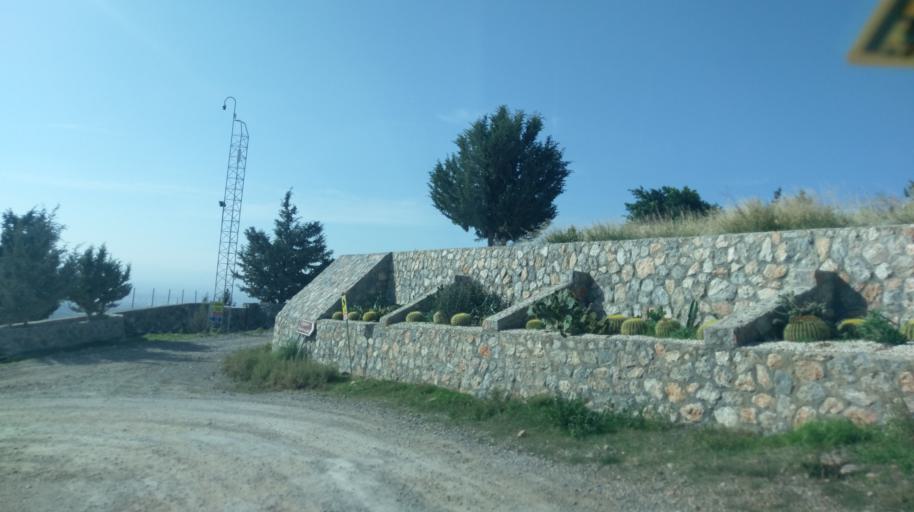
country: CY
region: Keryneia
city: Kyrenia
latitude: 35.2773
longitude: 33.3852
